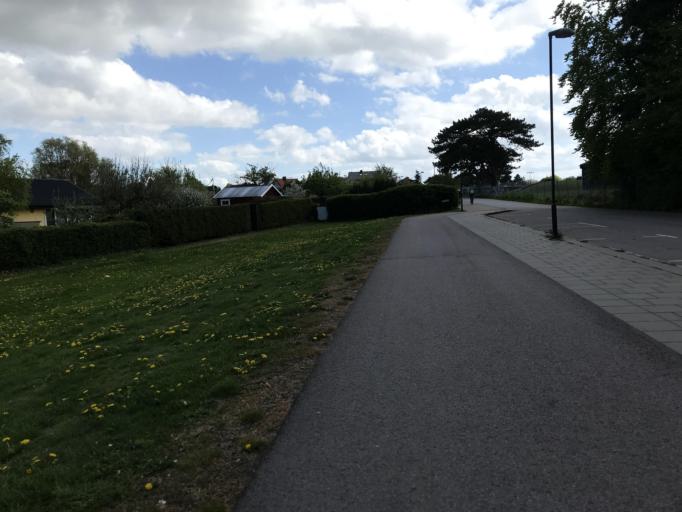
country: SE
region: Skane
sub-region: Landskrona
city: Landskrona
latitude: 55.8845
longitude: 12.8201
